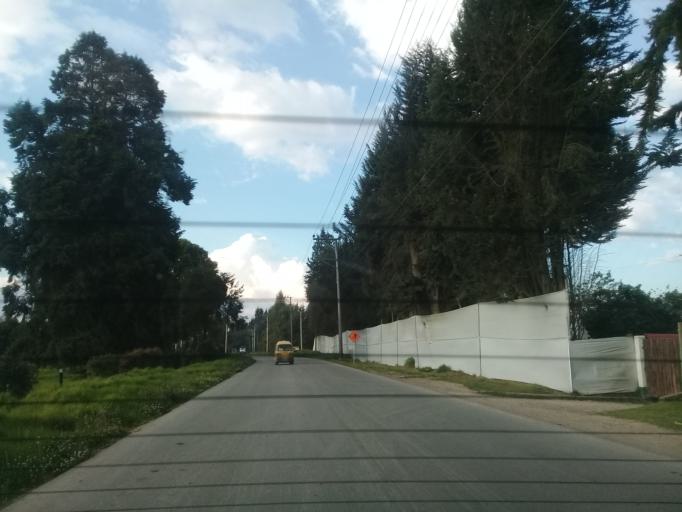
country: CO
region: Cundinamarca
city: Madrid
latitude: 4.7593
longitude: -74.2641
